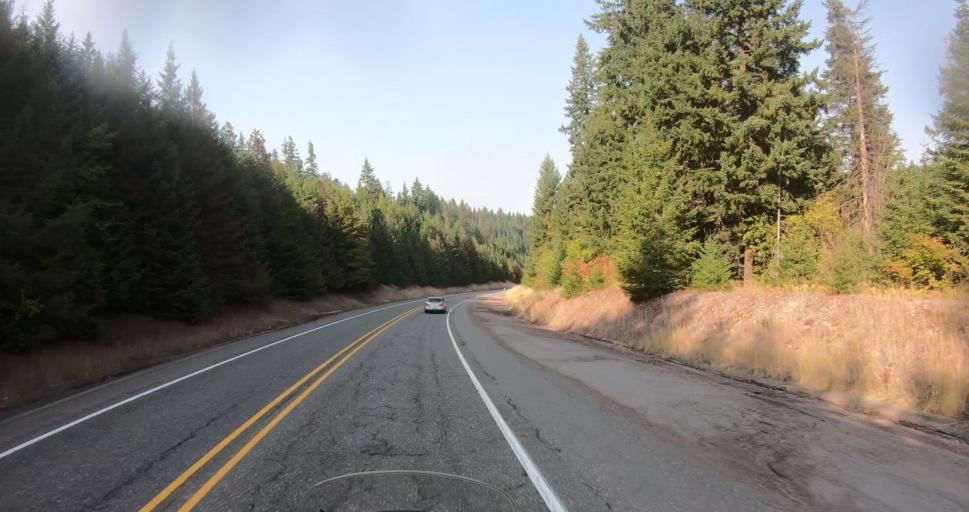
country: US
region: Oregon
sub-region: Hood River County
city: Odell
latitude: 45.4546
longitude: -121.5823
